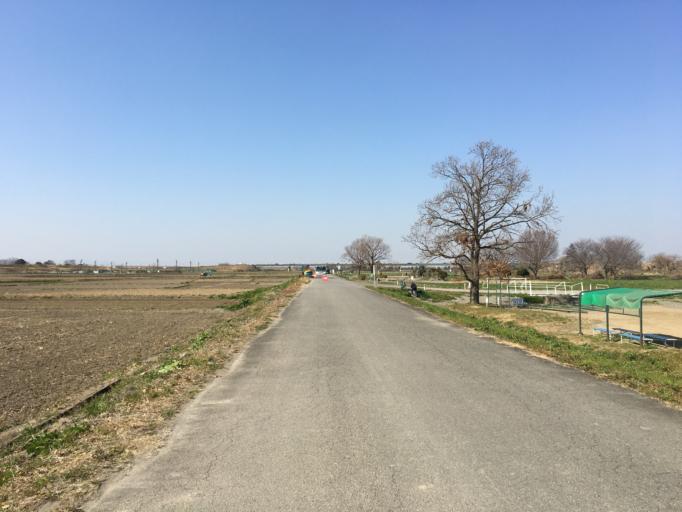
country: JP
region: Saitama
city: Shiki
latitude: 35.8480
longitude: 139.5950
